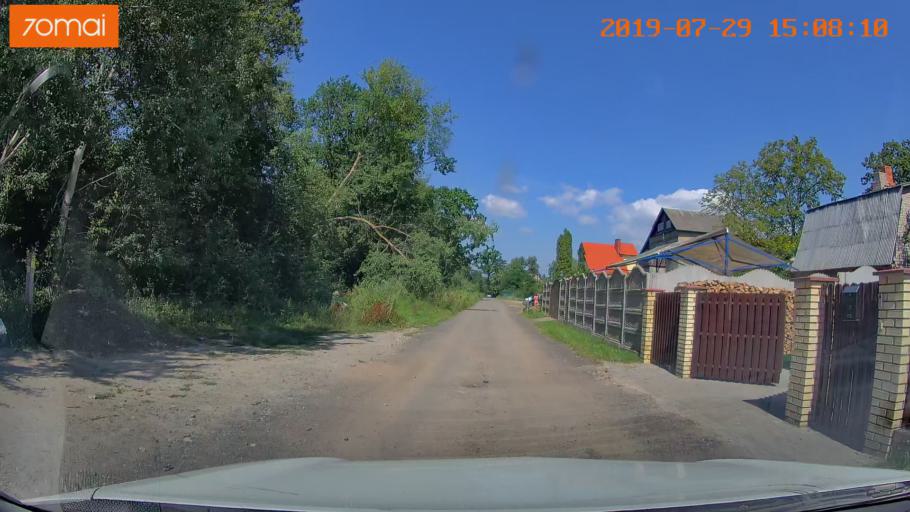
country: RU
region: Kaliningrad
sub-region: Gorod Kaliningrad
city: Baltiysk
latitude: 54.6789
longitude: 19.9154
